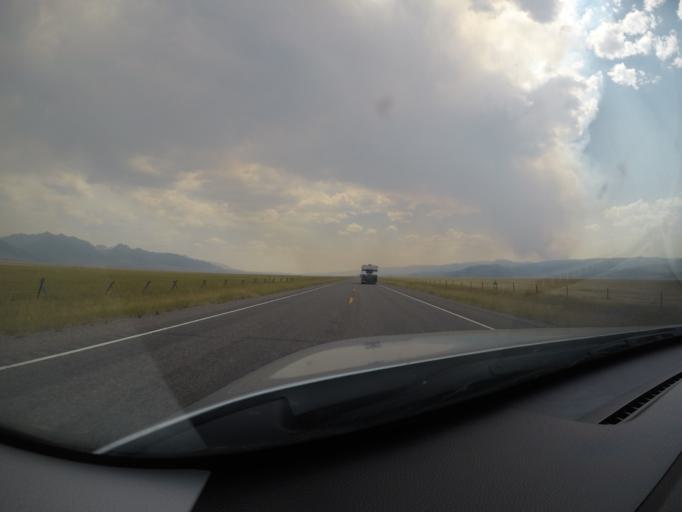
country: US
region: Montana
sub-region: Madison County
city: Virginia City
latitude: 45.1533
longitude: -111.6786
